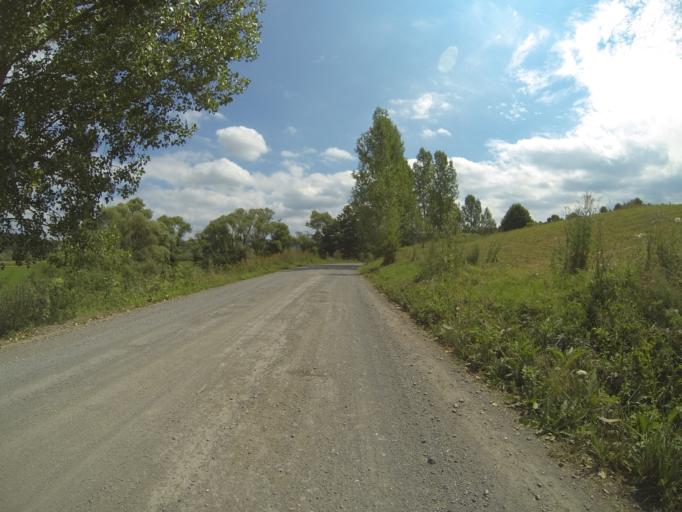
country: RO
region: Brasov
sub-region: Comuna Hoghiz
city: Hoghiz
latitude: 45.9780
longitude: 25.3696
